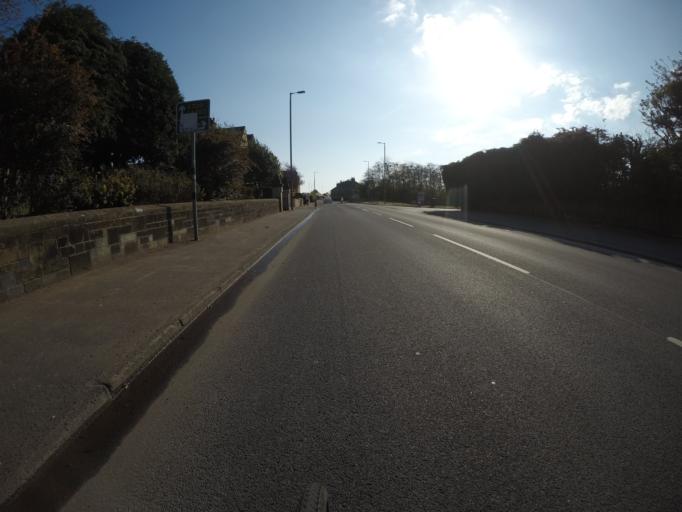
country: GB
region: Scotland
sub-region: North Ayrshire
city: Kilwinning
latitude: 55.6539
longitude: -4.7136
